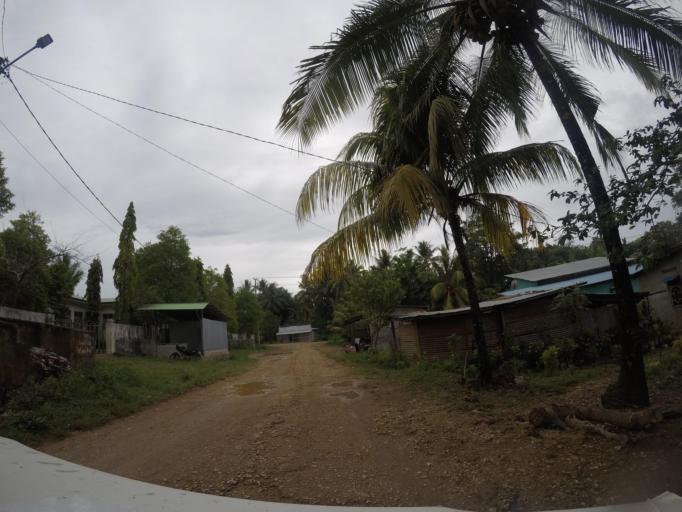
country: TL
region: Lautem
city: Lospalos
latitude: -8.5330
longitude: 126.9980
